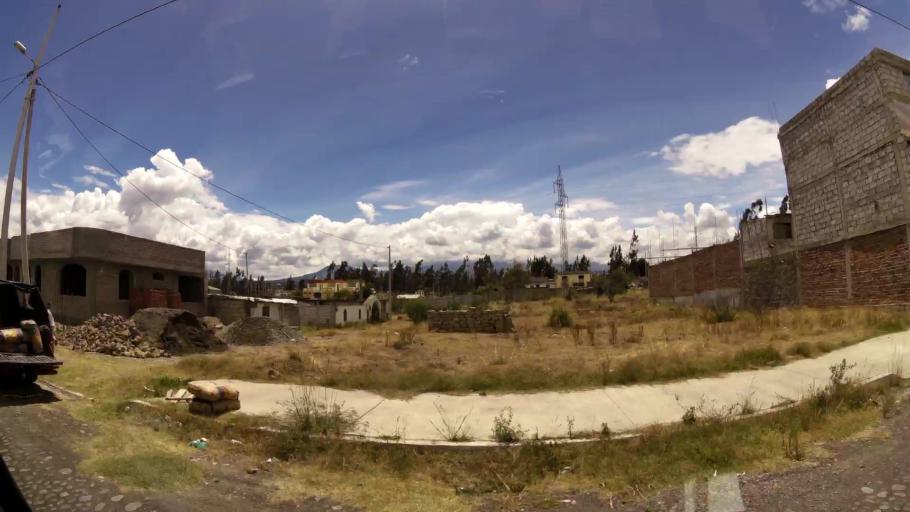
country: EC
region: Tungurahua
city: Ambato
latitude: -1.2771
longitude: -78.5986
